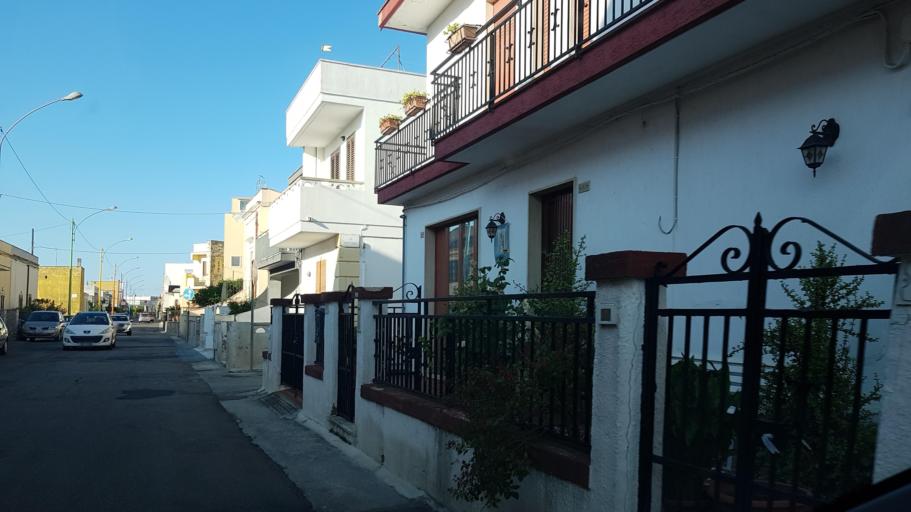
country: IT
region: Apulia
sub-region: Provincia di Lecce
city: Andrano
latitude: 39.9853
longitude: 18.3803
